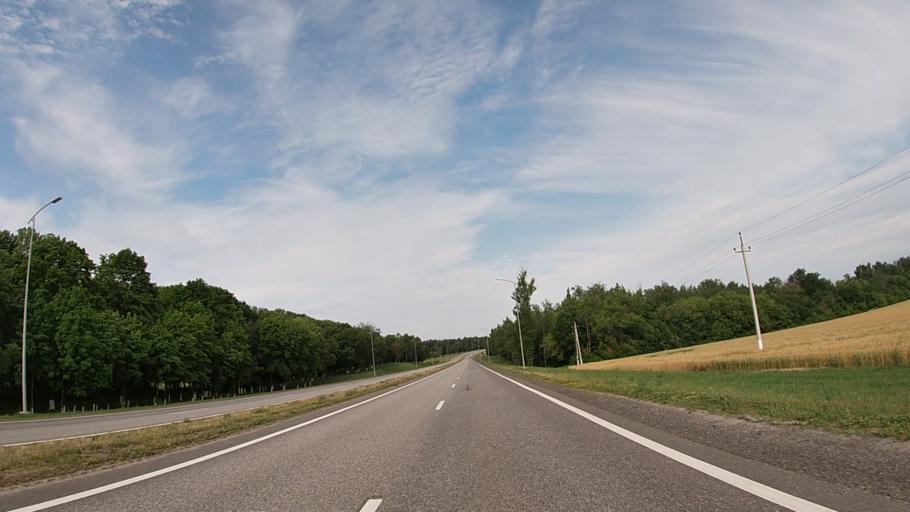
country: RU
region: Belgorod
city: Borisovka
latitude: 50.7503
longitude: 35.9981
